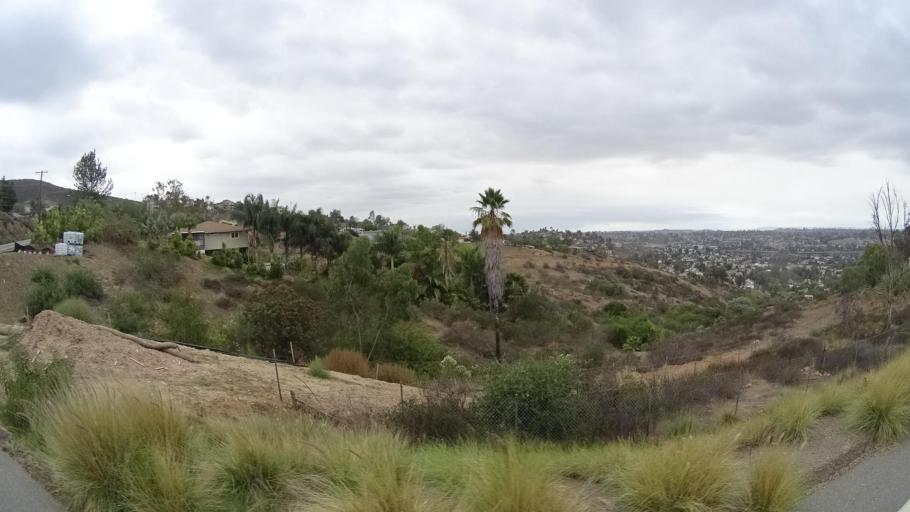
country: US
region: California
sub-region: San Diego County
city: Spring Valley
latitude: 32.7314
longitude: -116.9980
